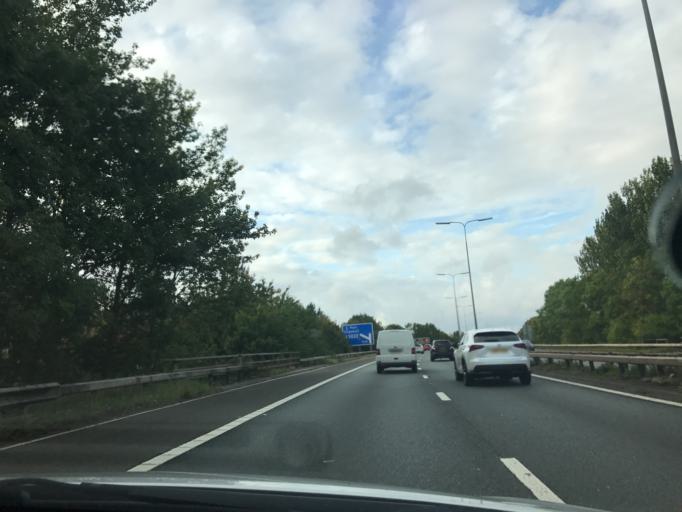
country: GB
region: England
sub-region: Cheshire West and Chester
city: Ellesmere Port
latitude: 53.2762
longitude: -2.8837
